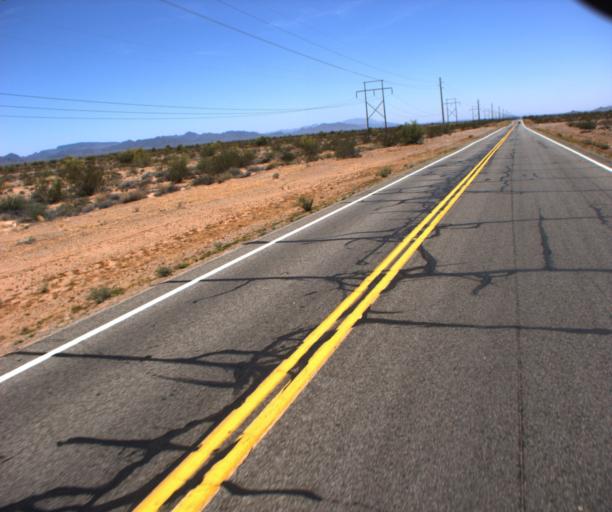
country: US
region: Arizona
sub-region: La Paz County
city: Quartzsite
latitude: 33.7969
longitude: -114.2170
